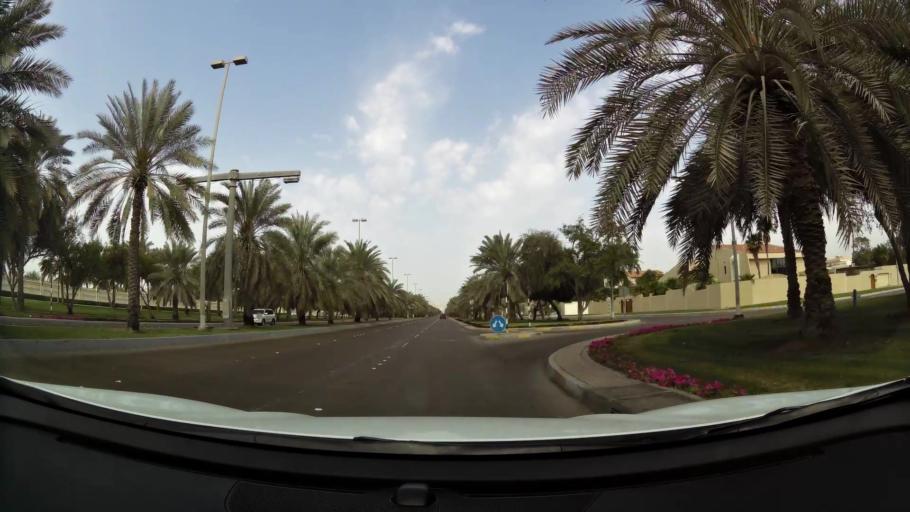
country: AE
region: Abu Dhabi
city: Abu Dhabi
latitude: 24.4363
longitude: 54.3657
